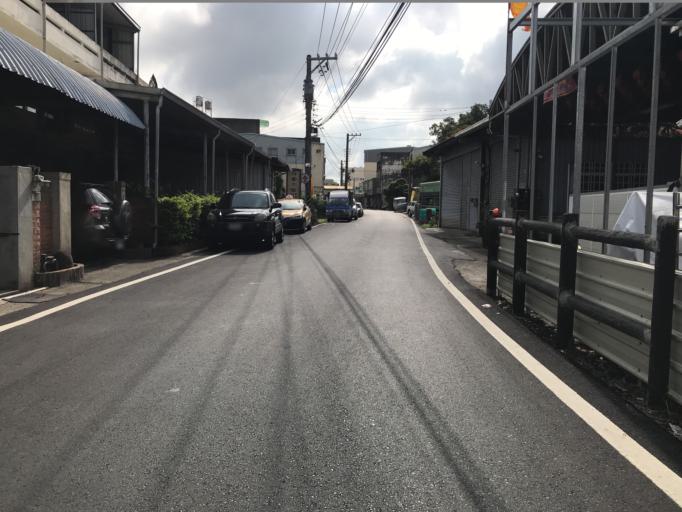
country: TW
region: Taiwan
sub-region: Hsinchu
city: Zhubei
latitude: 24.8089
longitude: 121.0049
